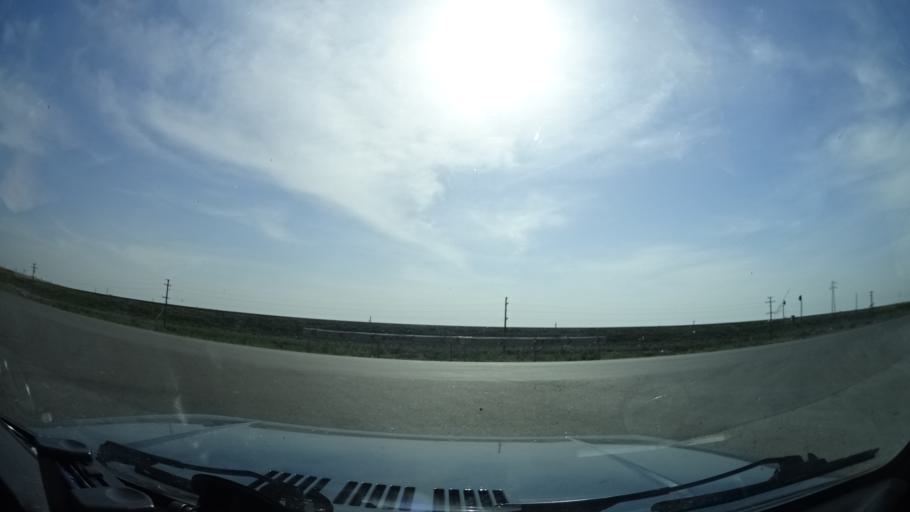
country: AZ
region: Salyan
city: Salyan
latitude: 39.6215
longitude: 48.9460
